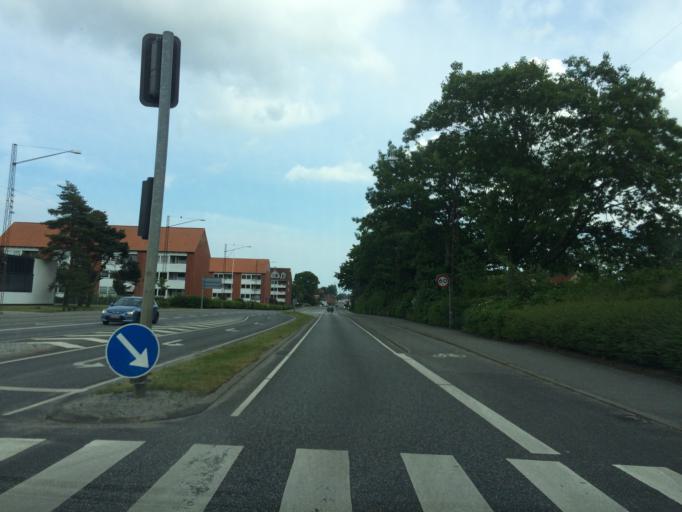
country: DK
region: South Denmark
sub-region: Middelfart Kommune
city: Middelfart
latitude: 55.5011
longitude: 9.7265
